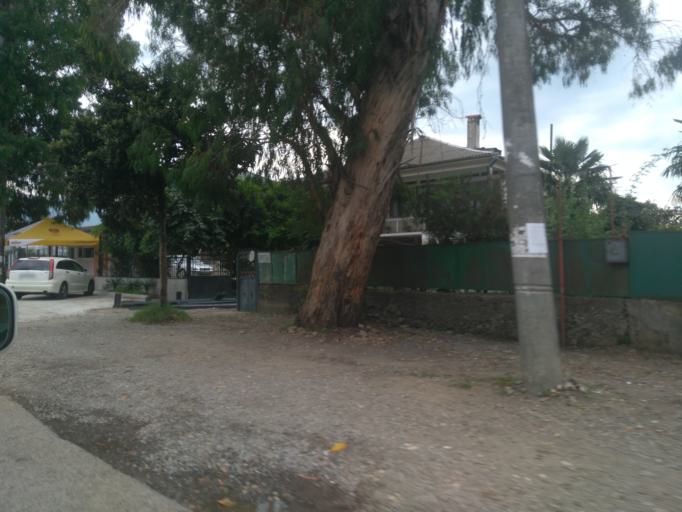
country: GE
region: Ajaria
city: Batumi
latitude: 41.6034
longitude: 41.6310
